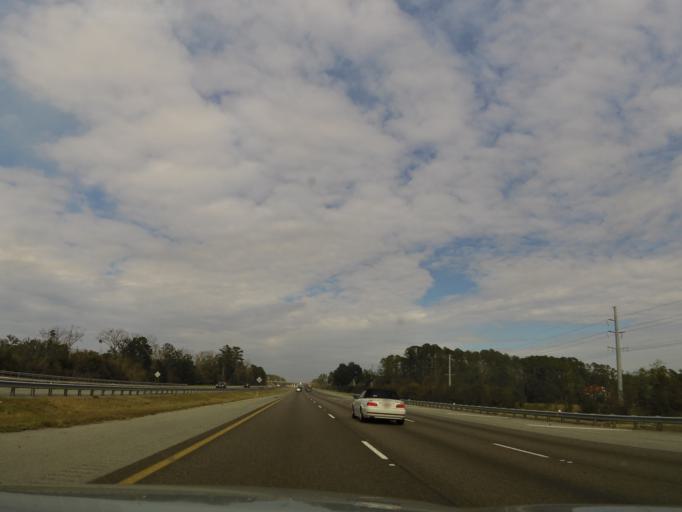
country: US
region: Georgia
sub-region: Liberty County
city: Midway
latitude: 31.8080
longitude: -81.3665
